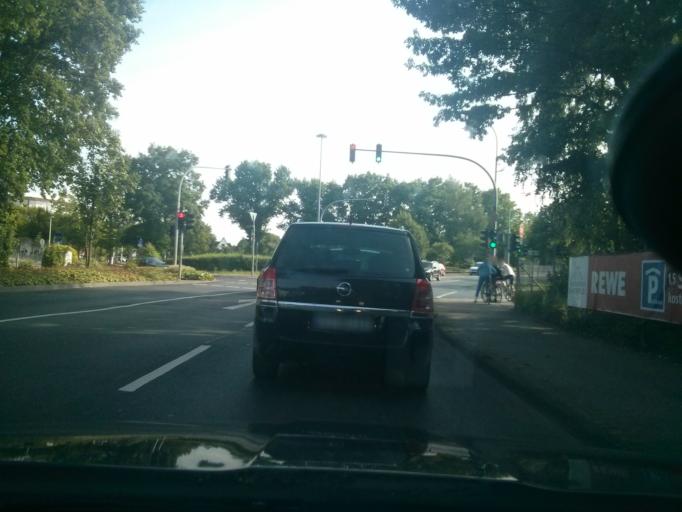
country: DE
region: Schleswig-Holstein
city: Halstenbek
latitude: 53.6039
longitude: 9.8361
